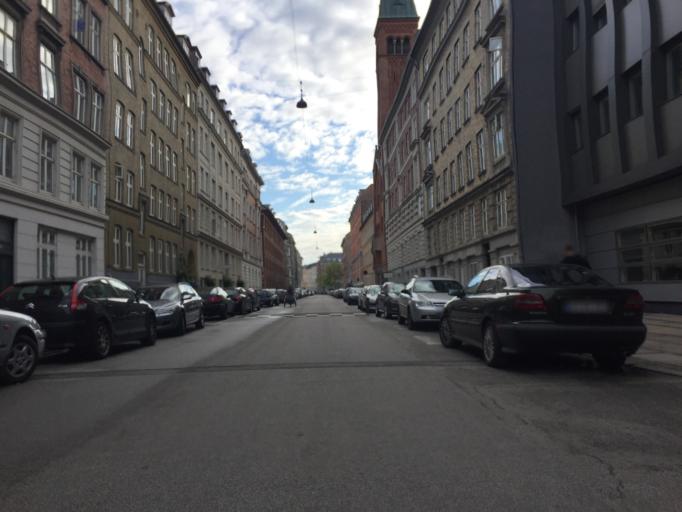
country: DK
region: Capital Region
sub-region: Kobenhavn
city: Copenhagen
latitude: 55.6976
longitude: 12.5763
